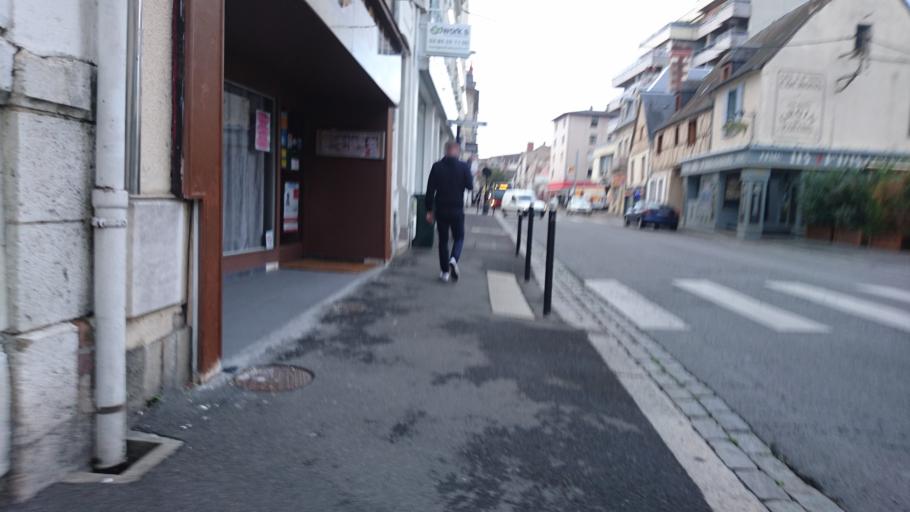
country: FR
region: Centre
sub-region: Departement du Cher
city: Bourges
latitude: 47.0886
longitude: 2.3931
